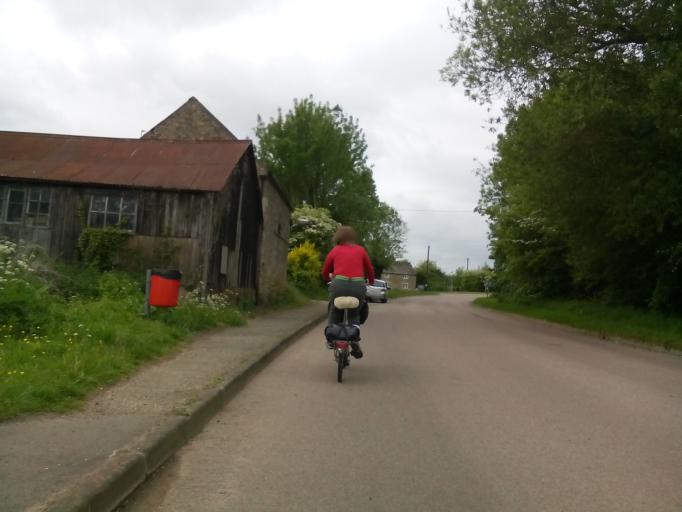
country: GB
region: England
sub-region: District of Rutland
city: South Luffenham
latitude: 52.5389
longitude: -0.5848
